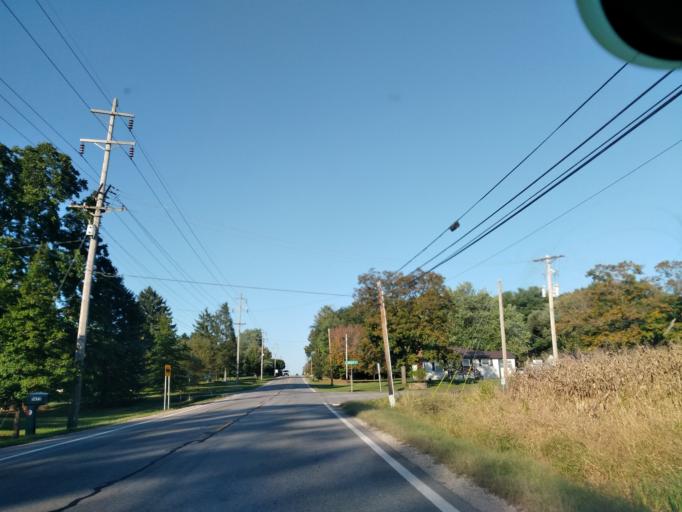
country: US
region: Ohio
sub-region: Fairfield County
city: Lancaster
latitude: 39.6472
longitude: -82.7260
